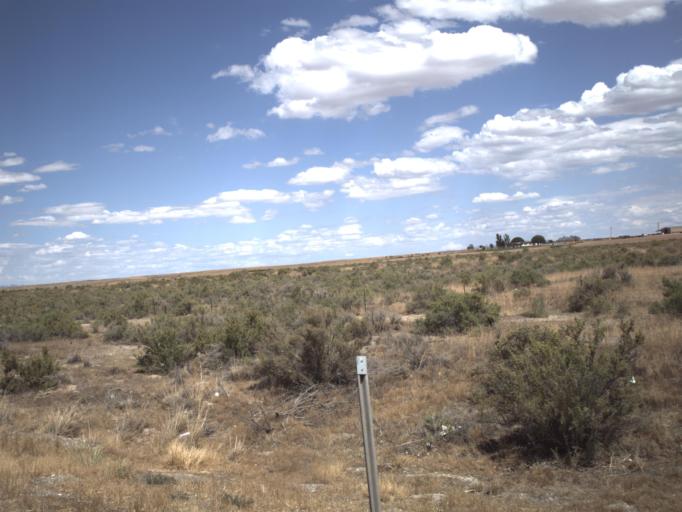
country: US
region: Utah
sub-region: Millard County
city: Delta
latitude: 39.3239
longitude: -112.4836
